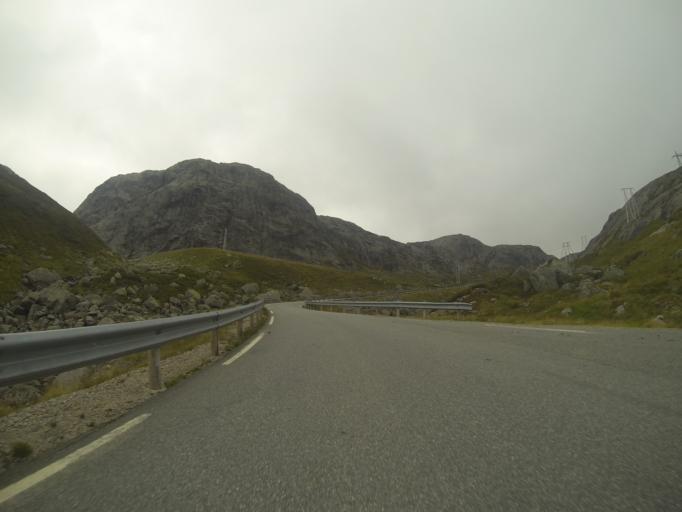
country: NO
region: Vest-Agder
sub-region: Sirdal
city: Tonstad
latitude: 59.0291
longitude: 6.6577
